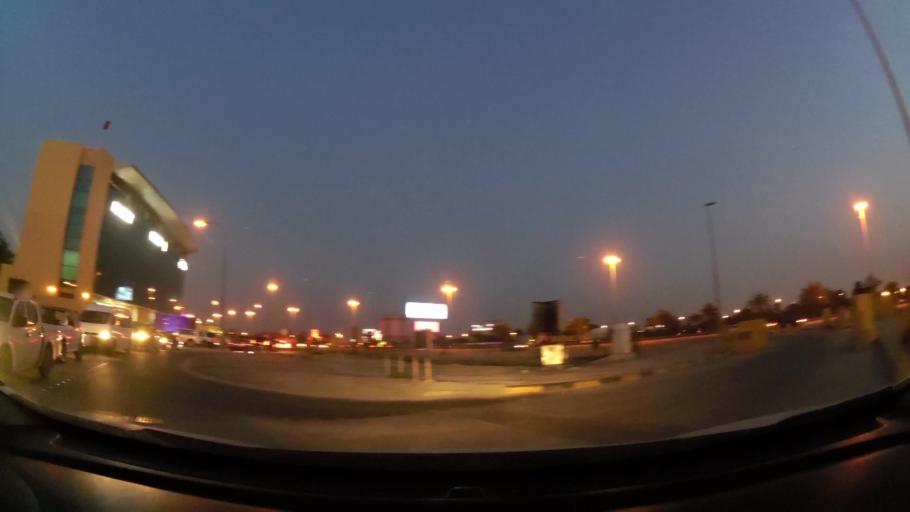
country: BH
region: Manama
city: Jidd Hafs
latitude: 26.1987
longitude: 50.5530
